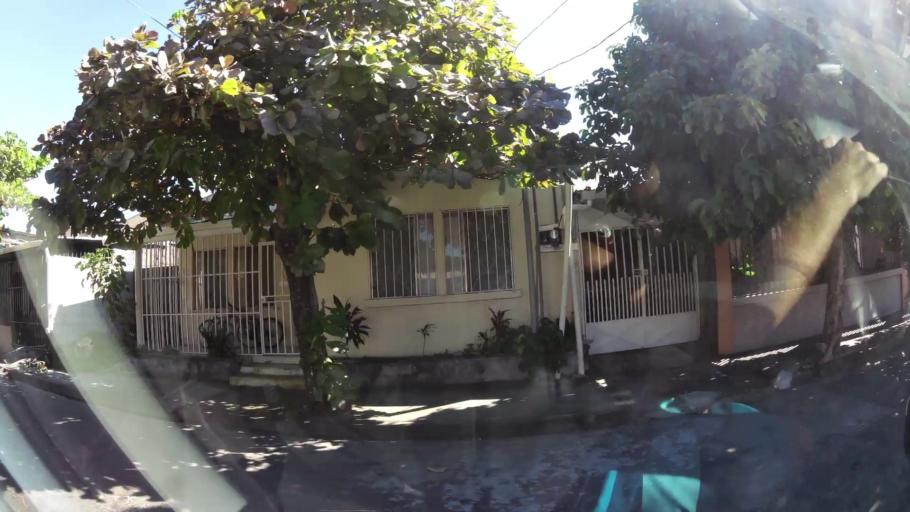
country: CR
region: Guanacaste
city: Liberia
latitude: 10.6334
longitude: -85.4352
